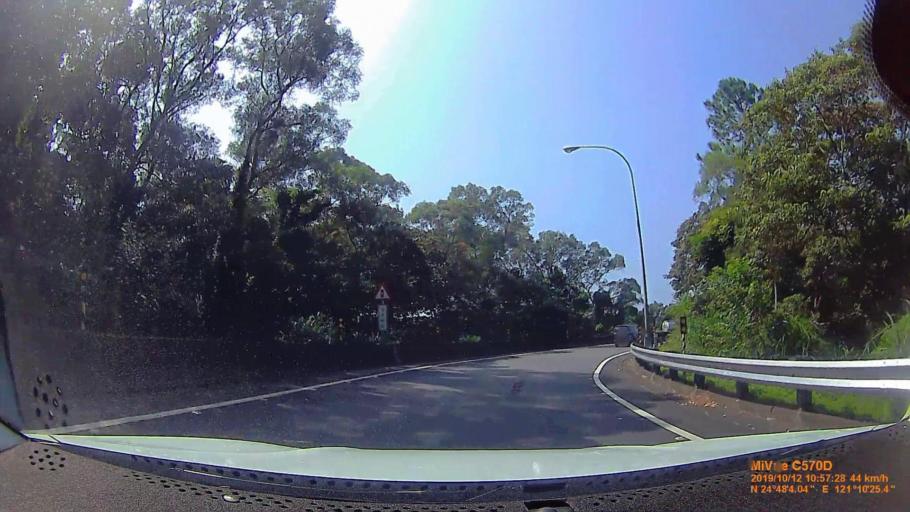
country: TW
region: Taiwan
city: Daxi
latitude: 24.8013
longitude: 121.1737
